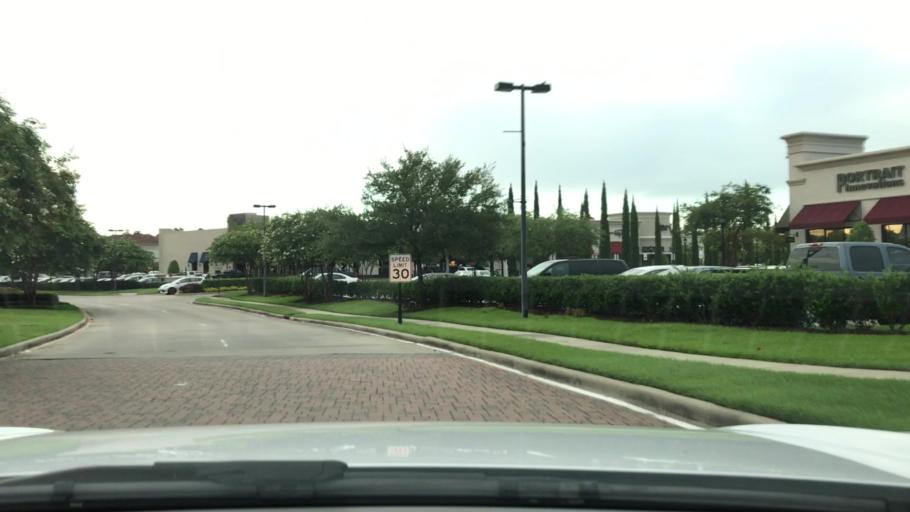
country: US
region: Louisiana
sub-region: East Baton Rouge Parish
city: Westminster
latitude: 30.4309
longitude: -91.1134
